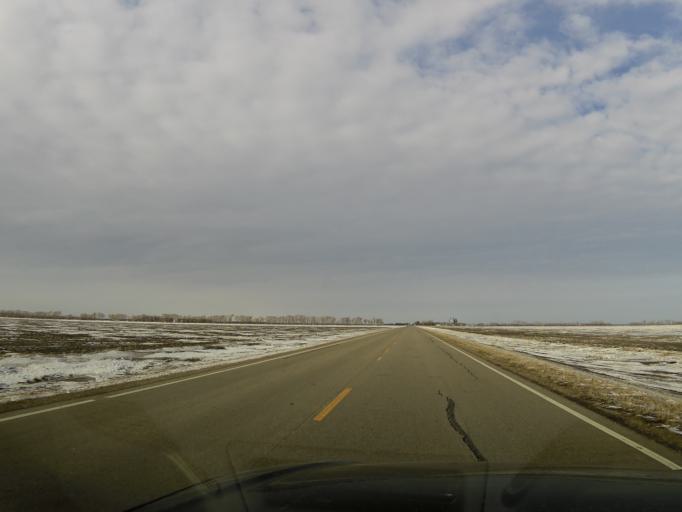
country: US
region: Minnesota
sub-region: Kittson County
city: Hallock
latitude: 48.5590
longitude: -97.1067
